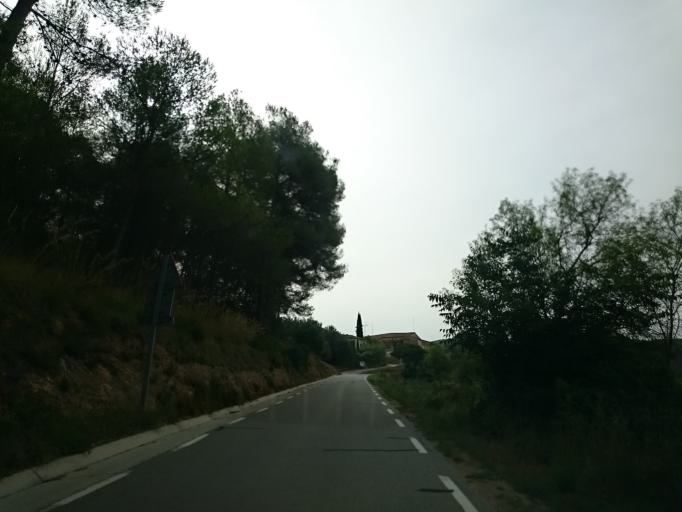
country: ES
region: Catalonia
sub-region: Provincia de Barcelona
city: Olivella
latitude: 41.3130
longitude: 1.7893
